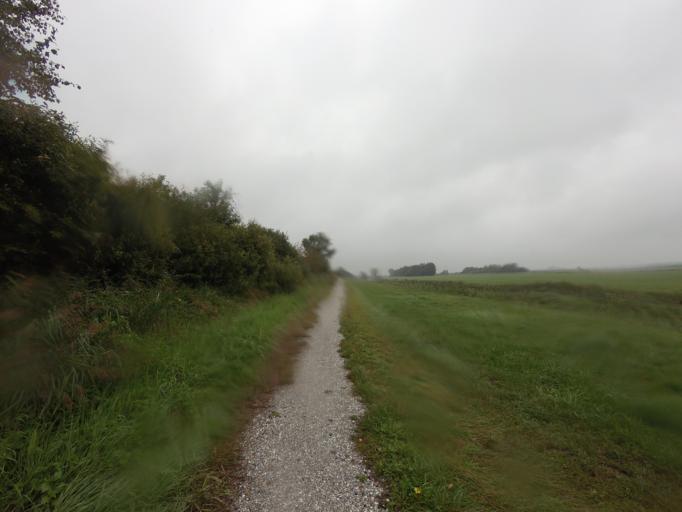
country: NL
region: Friesland
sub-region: Gemeente Smallingerland
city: Oudega
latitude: 53.0960
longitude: 5.9818
